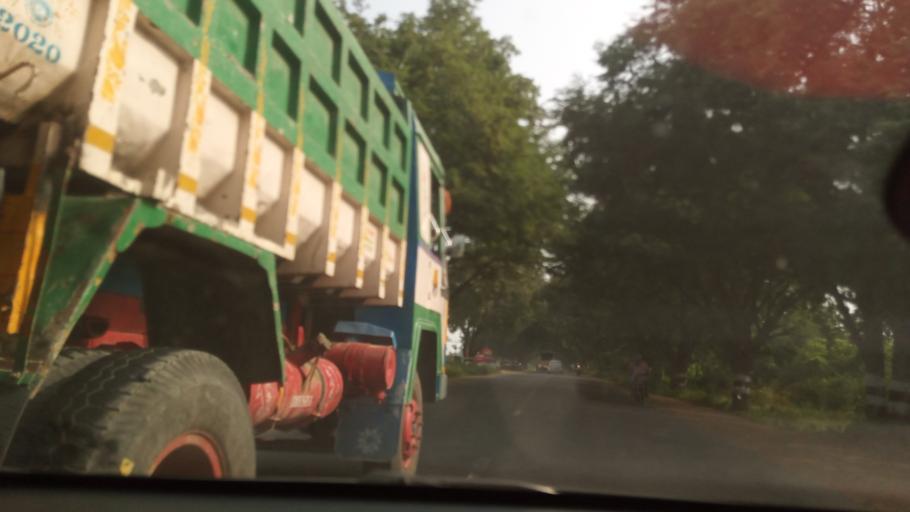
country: IN
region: Tamil Nadu
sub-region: Coimbatore
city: Annur
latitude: 11.1940
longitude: 77.0679
